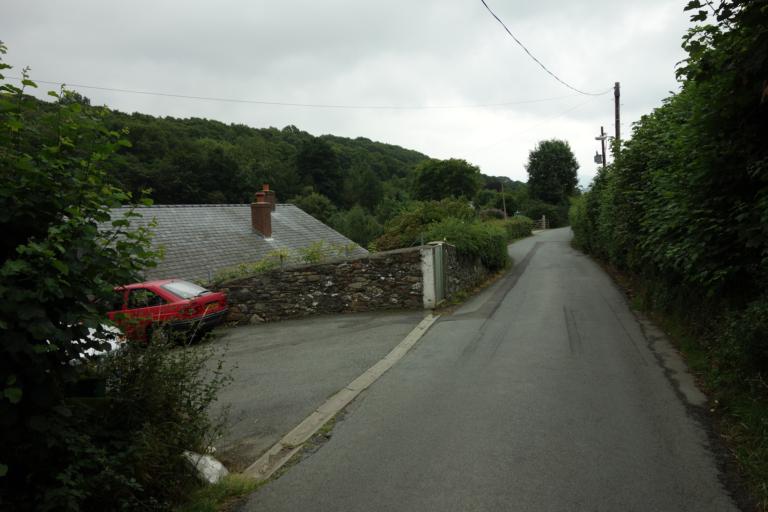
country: GB
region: Wales
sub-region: Conwy
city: Conwy
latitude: 53.2736
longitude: -3.8407
